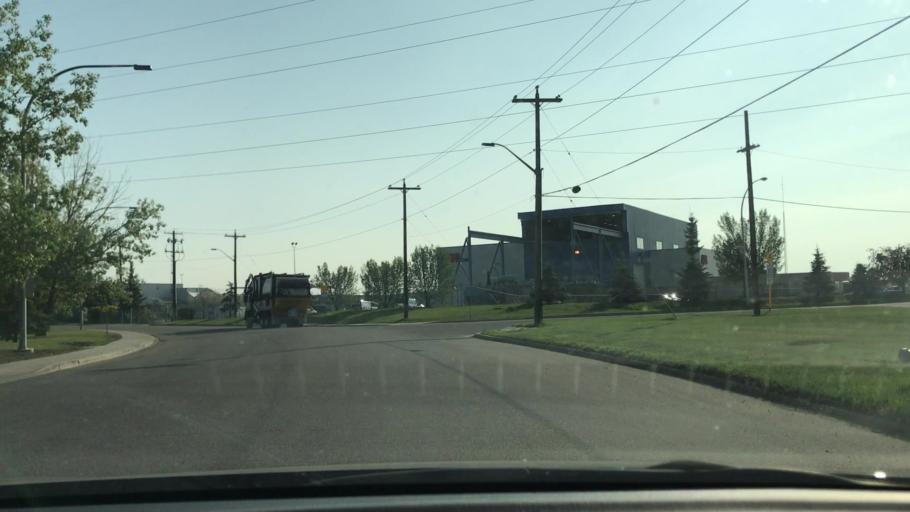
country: CA
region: Alberta
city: Edmonton
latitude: 53.4628
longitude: -113.4807
